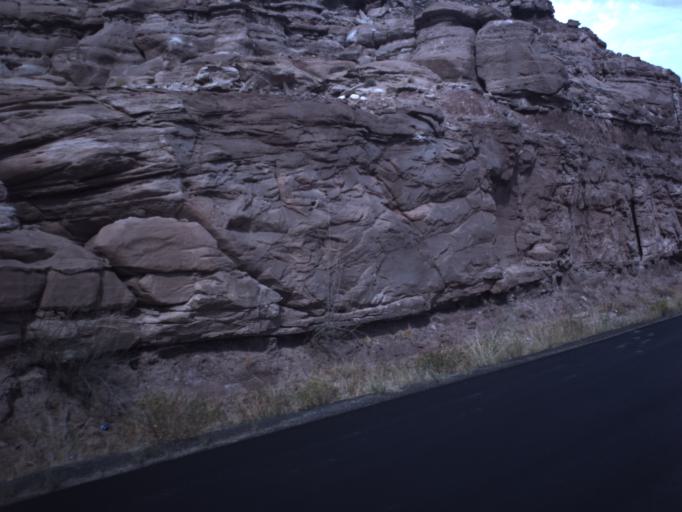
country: US
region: Utah
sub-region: San Juan County
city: Blanding
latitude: 37.2574
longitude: -109.2860
